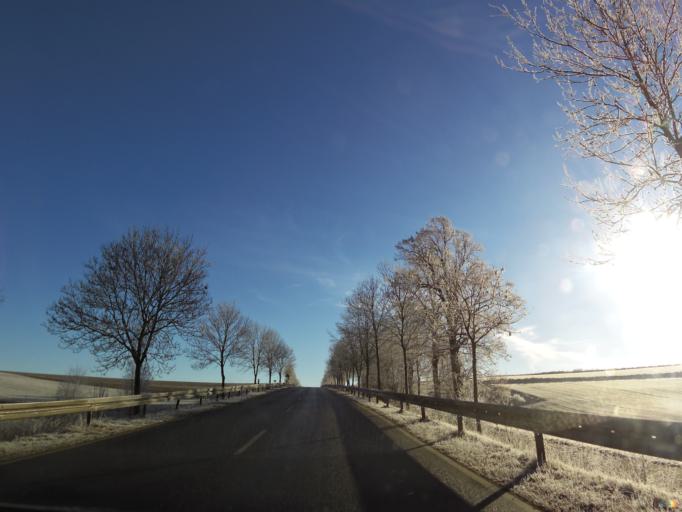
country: DE
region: Bavaria
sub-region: Upper Franconia
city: Wunsiedel
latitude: 50.0289
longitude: 12.0086
